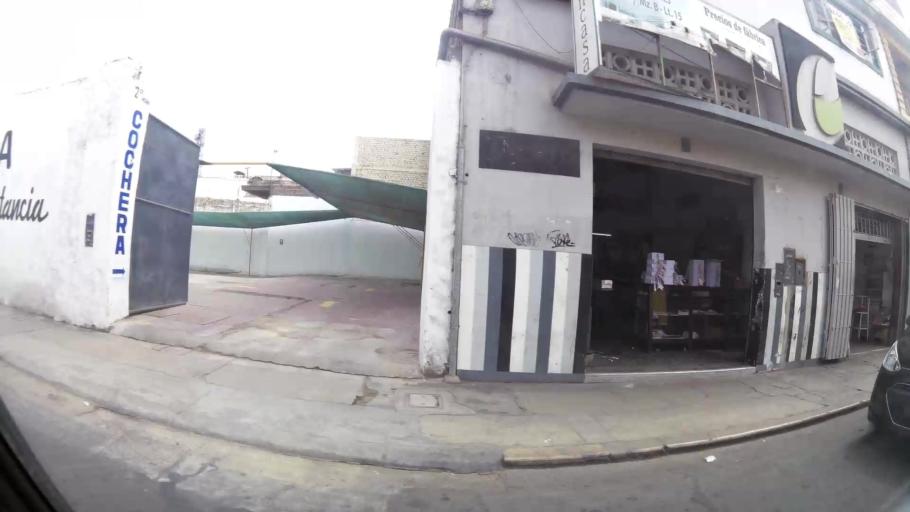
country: PE
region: La Libertad
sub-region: Provincia de Trujillo
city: Trujillo
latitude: -8.1091
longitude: -79.0242
